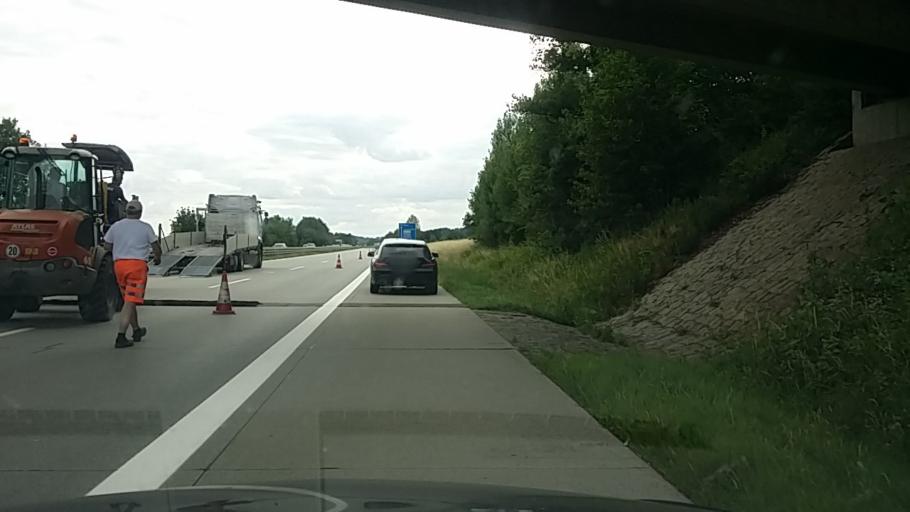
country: DE
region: Bavaria
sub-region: Lower Bavaria
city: Ergolding
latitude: 48.5776
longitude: 12.1454
